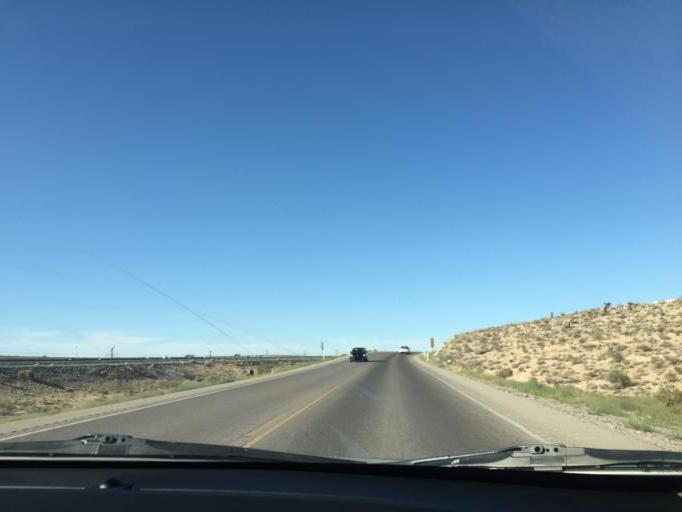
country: US
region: Nevada
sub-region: Clark County
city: Enterprise
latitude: 35.8643
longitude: -115.2466
